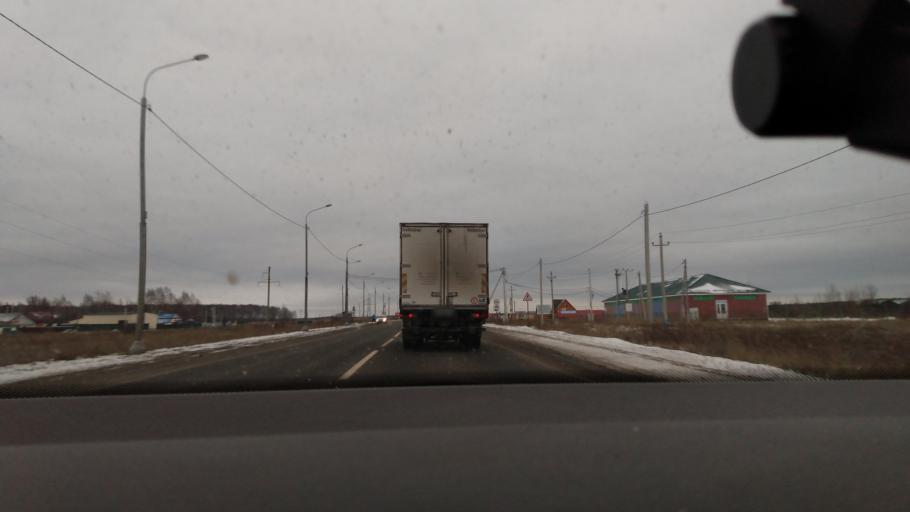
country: RU
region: Moskovskaya
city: Yegor'yevsk
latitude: 55.4054
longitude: 39.0555
